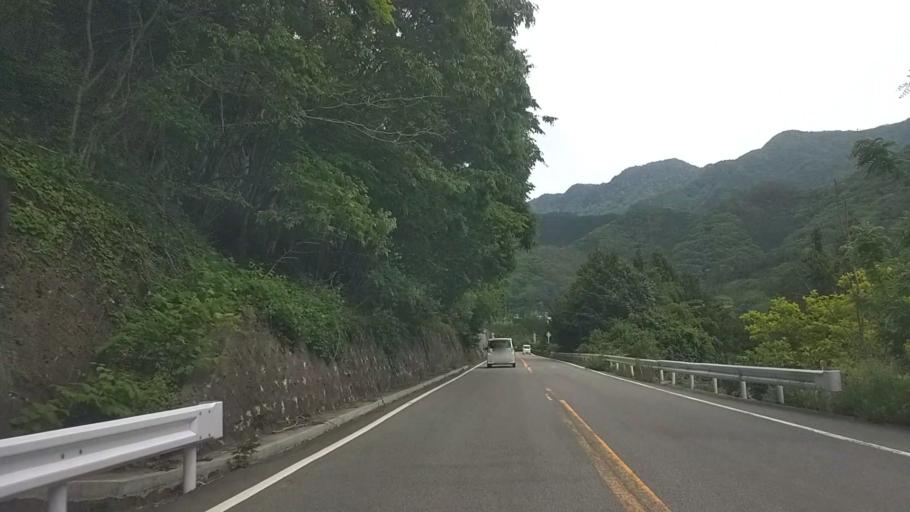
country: JP
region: Yamanashi
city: Fujikawaguchiko
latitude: 35.5307
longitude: 138.6167
